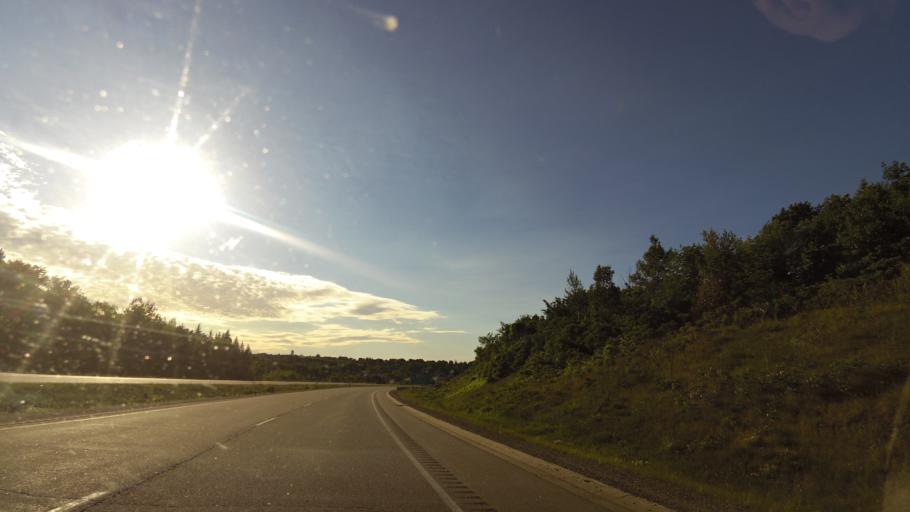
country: CA
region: Ontario
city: Midland
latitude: 44.7437
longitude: -79.6986
